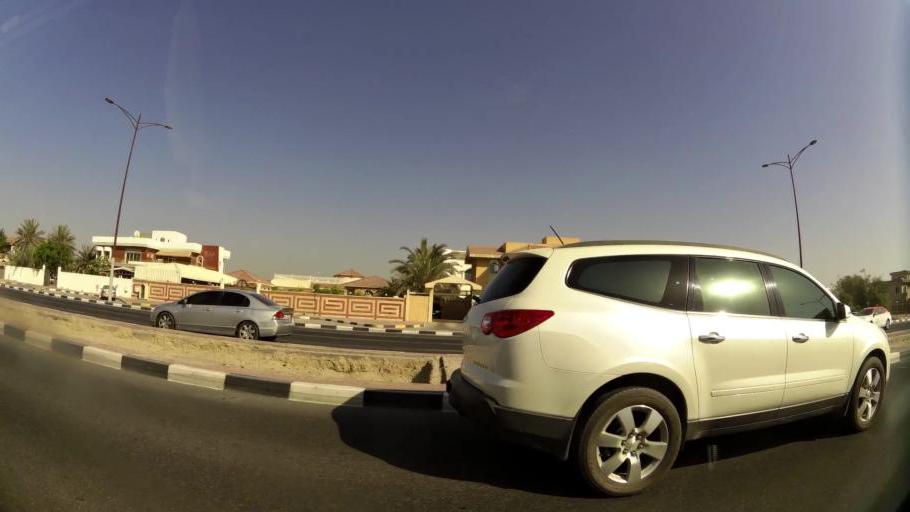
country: AE
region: Ash Shariqah
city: Sharjah
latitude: 25.3638
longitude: 55.4465
